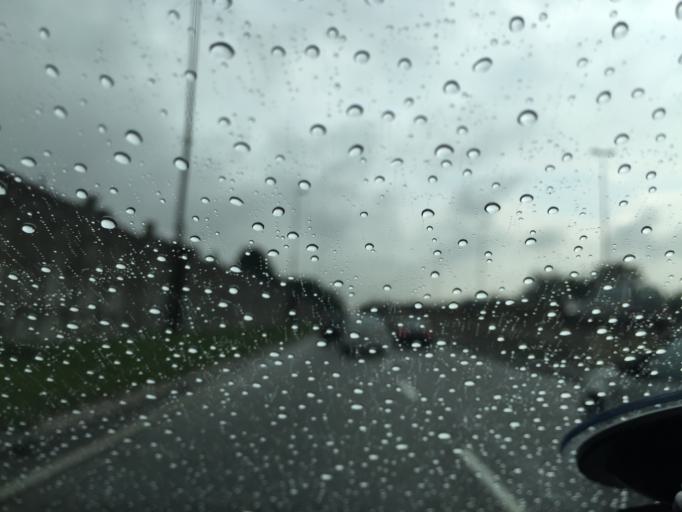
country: MY
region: Selangor
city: Subang Jaya
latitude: 3.0669
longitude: 101.5929
